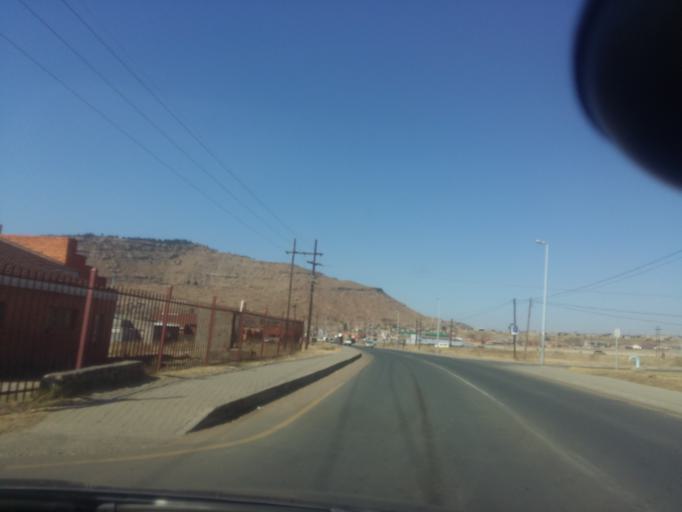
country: LS
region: Maseru
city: Maseru
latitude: -29.3455
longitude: 27.4534
